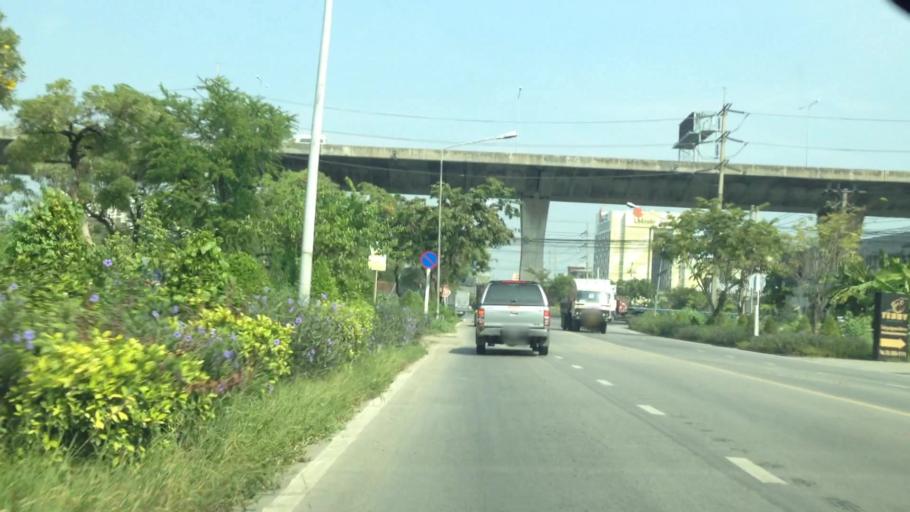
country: TH
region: Bangkok
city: Bang Na
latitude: 13.6644
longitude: 100.6453
